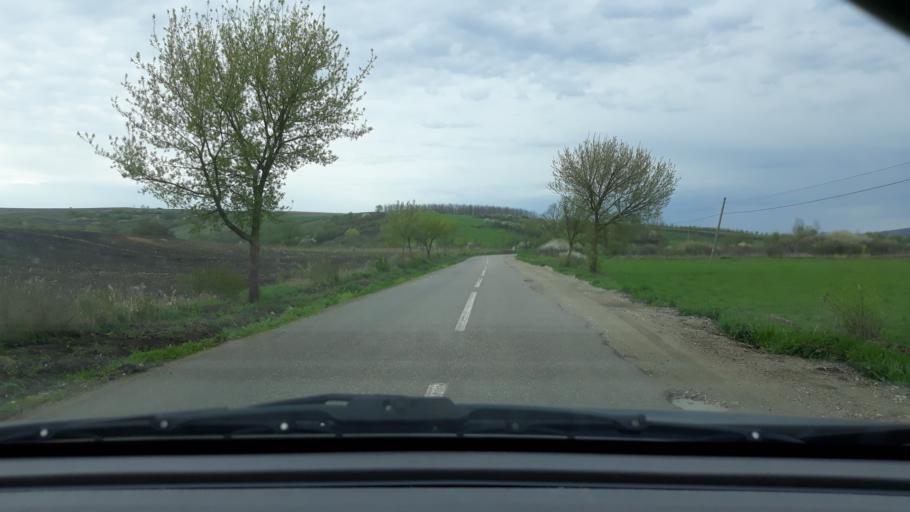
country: RO
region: Salaj
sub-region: Comuna Salatig
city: Salatig
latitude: 47.3848
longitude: 23.1476
